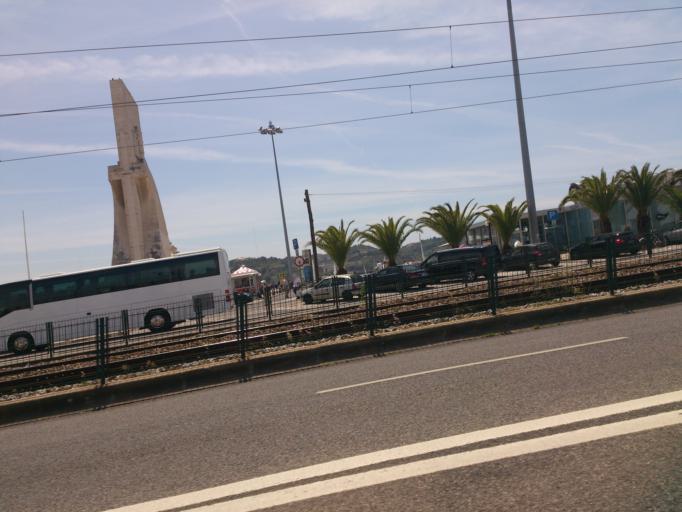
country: PT
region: Lisbon
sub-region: Oeiras
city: Alges
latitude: 38.6949
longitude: -9.2062
